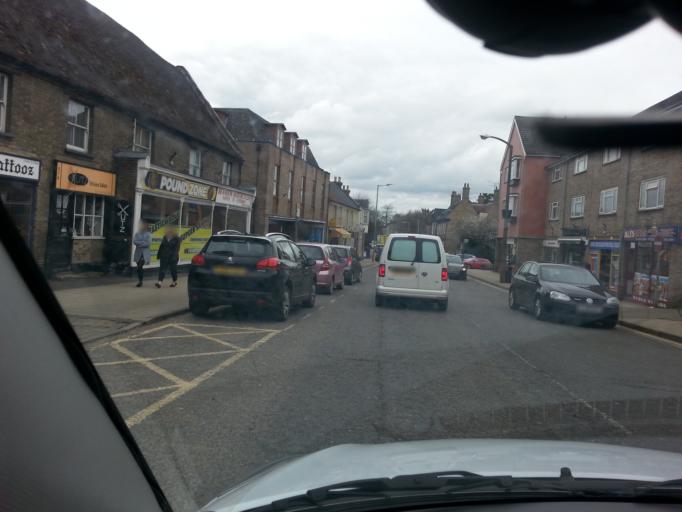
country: GB
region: England
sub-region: Norfolk
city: Weeting
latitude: 52.4488
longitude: 0.6235
